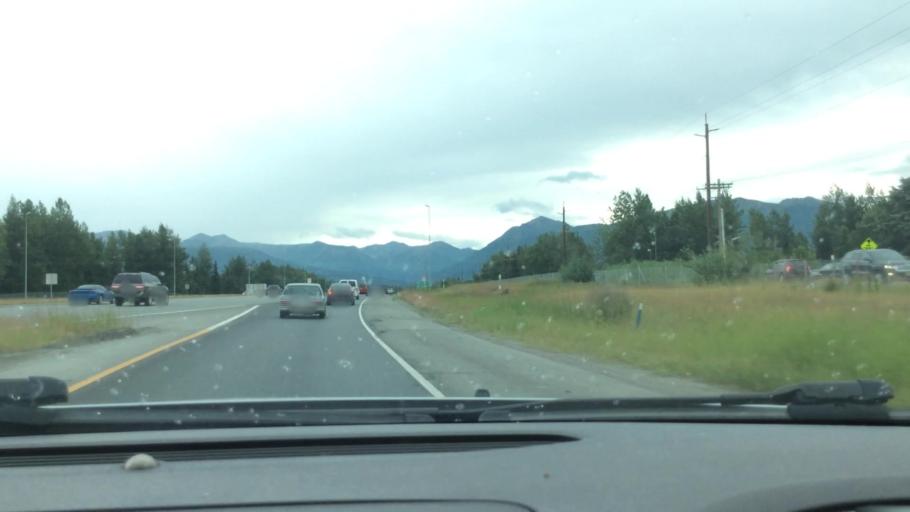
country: US
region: Alaska
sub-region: Anchorage Municipality
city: Anchorage
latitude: 61.2244
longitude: -149.7743
